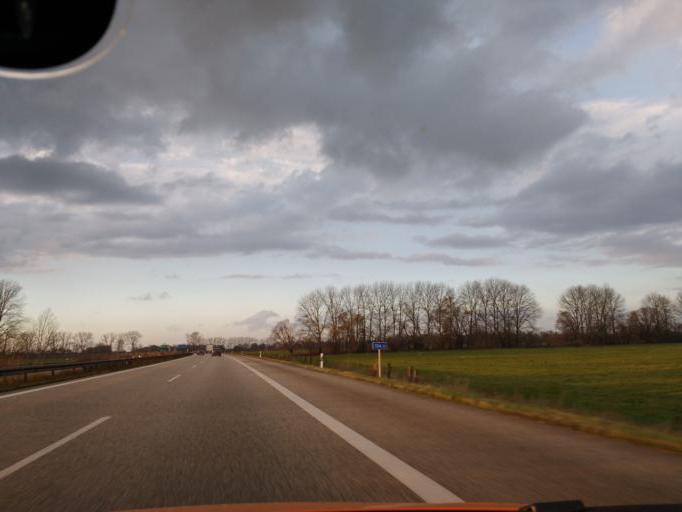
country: DE
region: Mecklenburg-Vorpommern
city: Neustadt-Glewe
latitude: 53.4077
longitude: 11.5668
